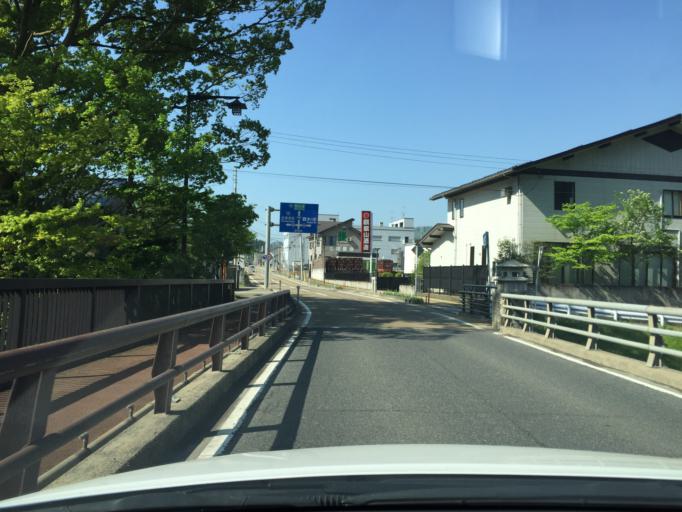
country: JP
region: Niigata
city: Suibara
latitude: 37.6810
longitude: 139.4612
